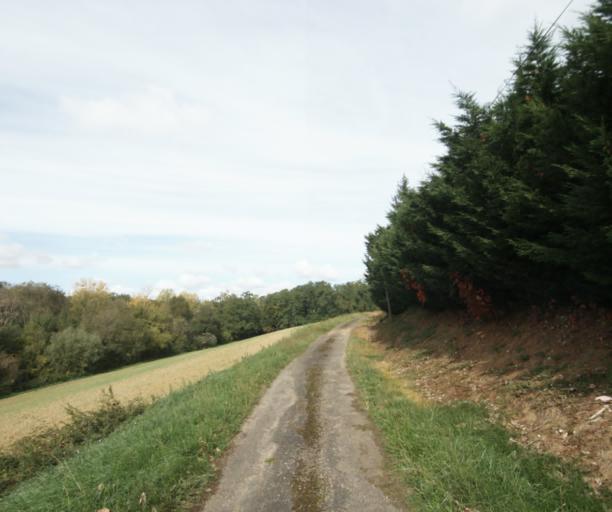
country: FR
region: Midi-Pyrenees
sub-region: Departement du Gers
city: Eauze
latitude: 43.8464
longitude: 0.1284
